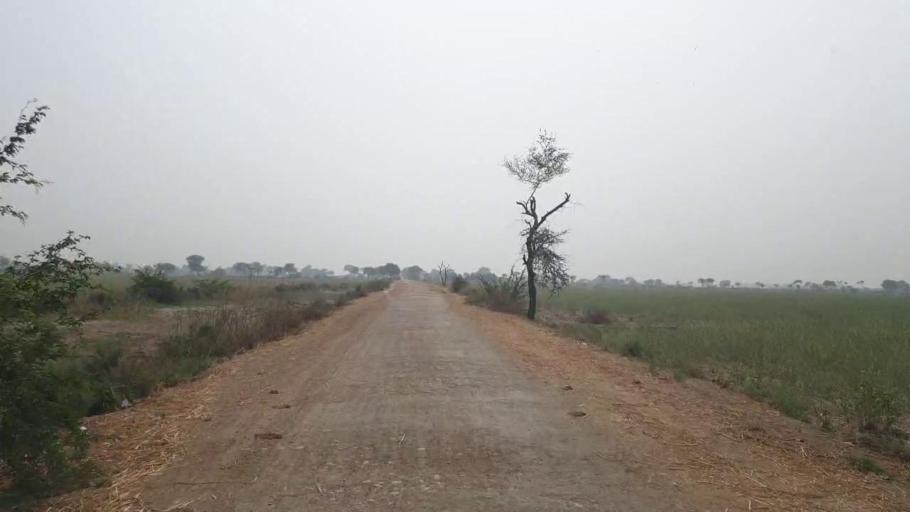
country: PK
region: Sindh
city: Kario
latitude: 24.6493
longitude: 68.6217
